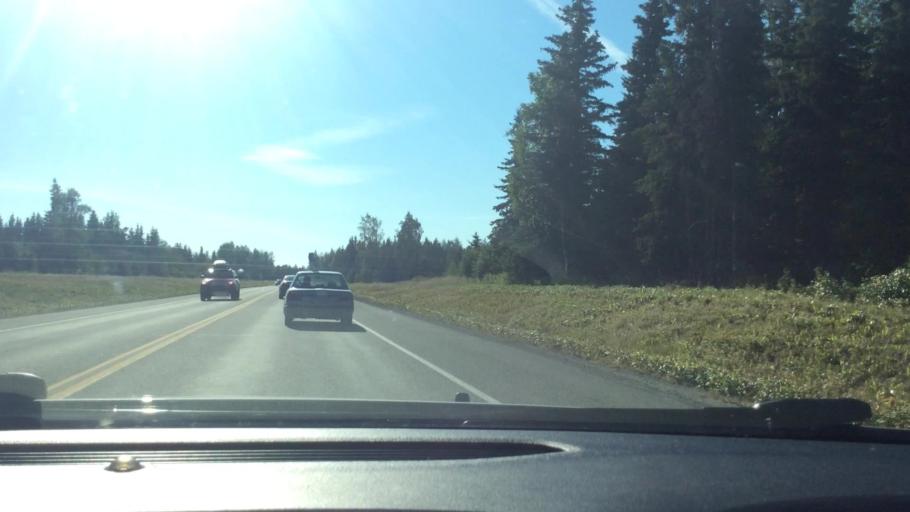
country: US
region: Alaska
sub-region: Anchorage Municipality
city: Elmendorf Air Force Base
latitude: 61.2398
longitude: -149.7180
